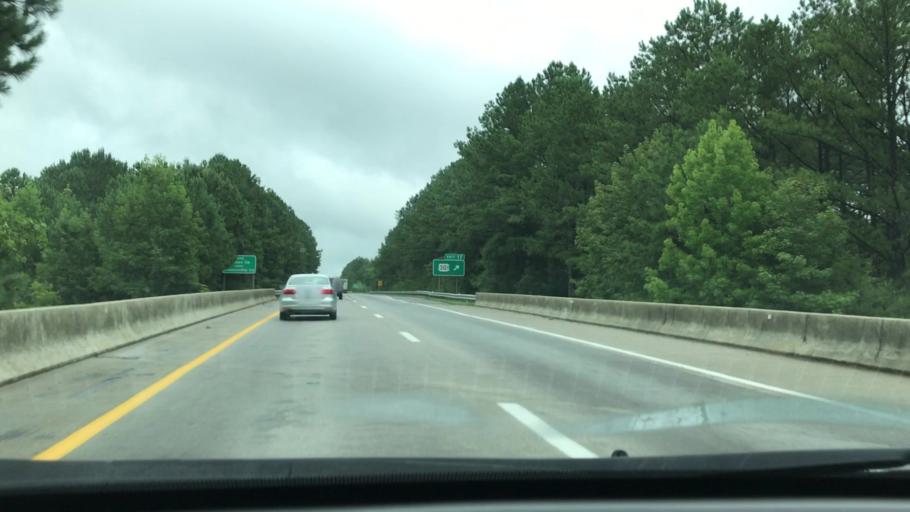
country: US
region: Virginia
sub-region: City of Emporia
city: Emporia
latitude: 36.7651
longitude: -77.4809
